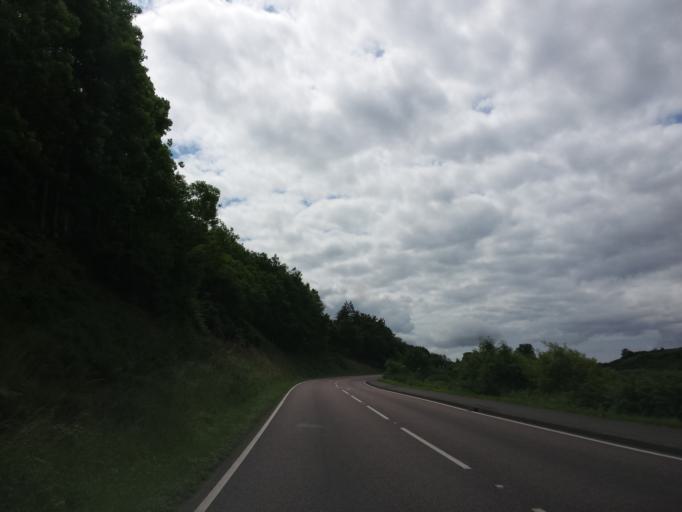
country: GB
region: Scotland
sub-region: Argyll and Bute
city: Oban
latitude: 56.4382
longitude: -5.4504
